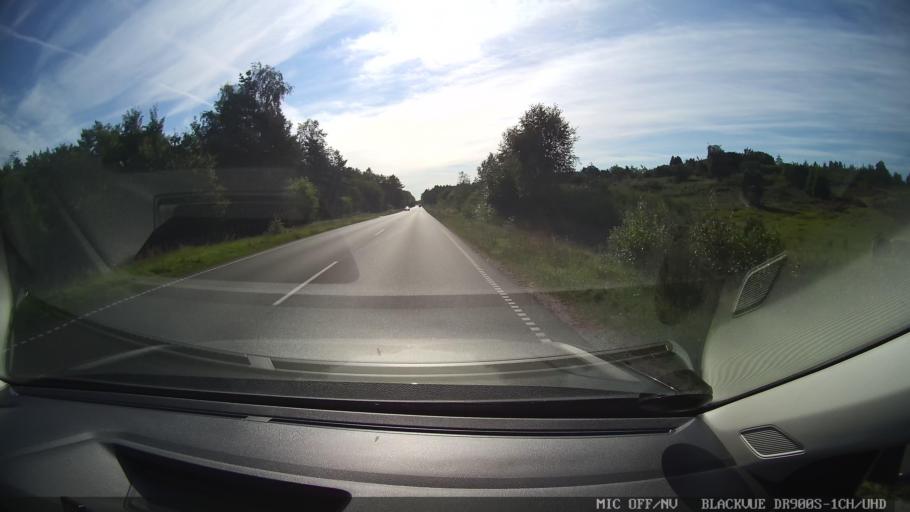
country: DK
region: North Denmark
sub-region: Mariagerfjord Kommune
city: Hadsund
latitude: 56.7302
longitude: 10.0845
